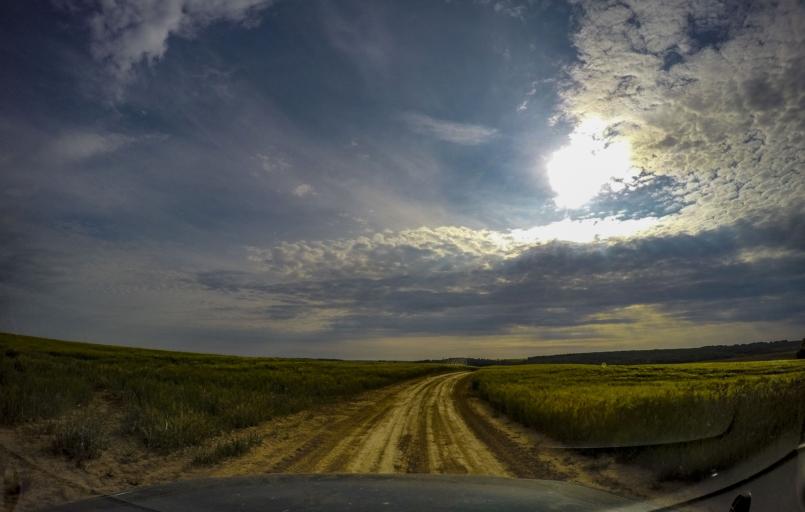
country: HU
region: Somogy
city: Karad
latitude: 46.6723
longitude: 17.8208
